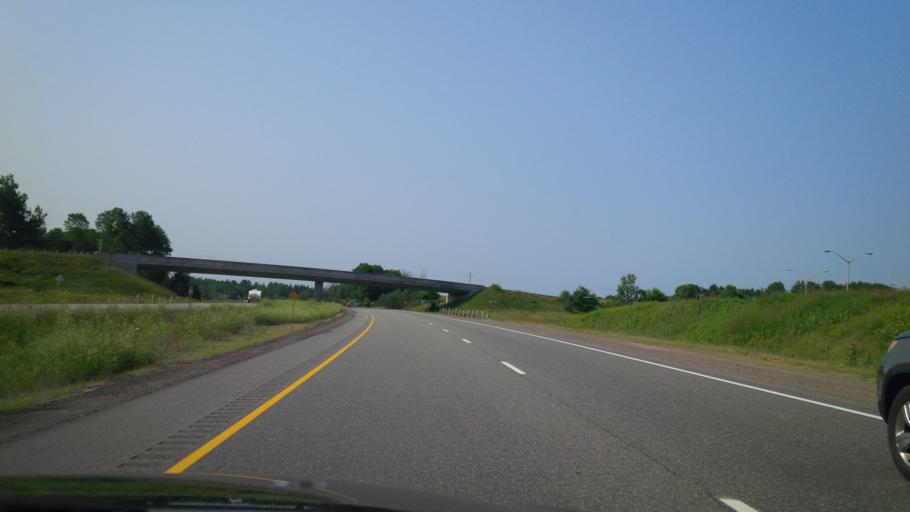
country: CA
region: Ontario
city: Bracebridge
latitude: 45.0367
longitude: -79.2923
